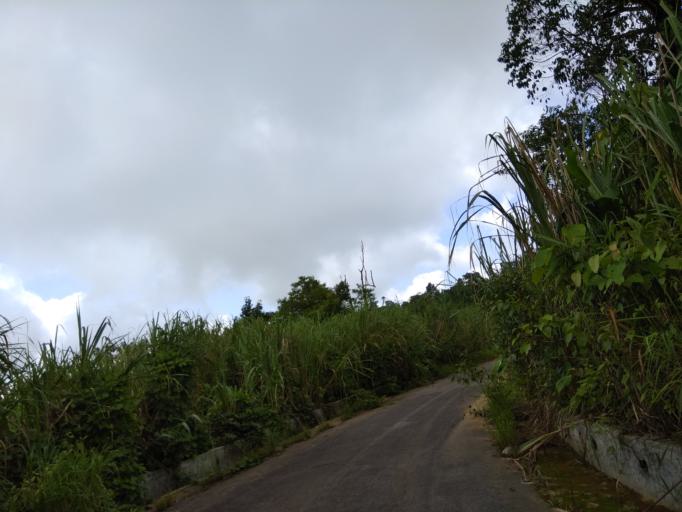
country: BD
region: Chittagong
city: Bandarban
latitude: 21.7374
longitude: 92.4203
